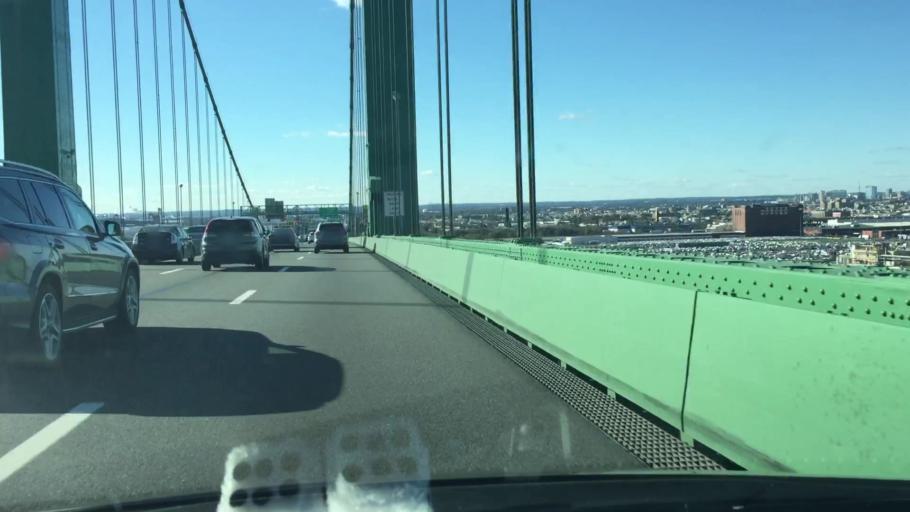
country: US
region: New Jersey
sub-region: Camden County
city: Gloucester City
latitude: 39.9057
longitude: -75.1318
